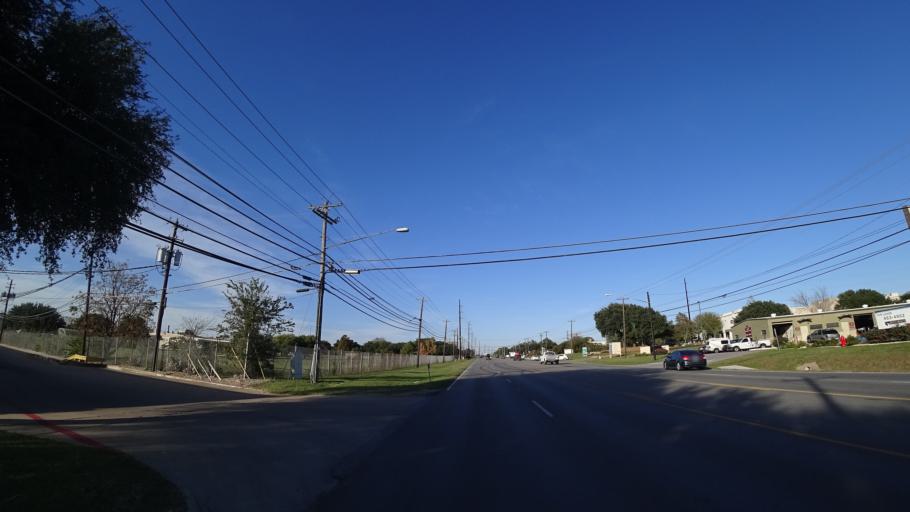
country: US
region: Texas
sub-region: Travis County
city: Wells Branch
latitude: 30.3809
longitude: -97.7248
